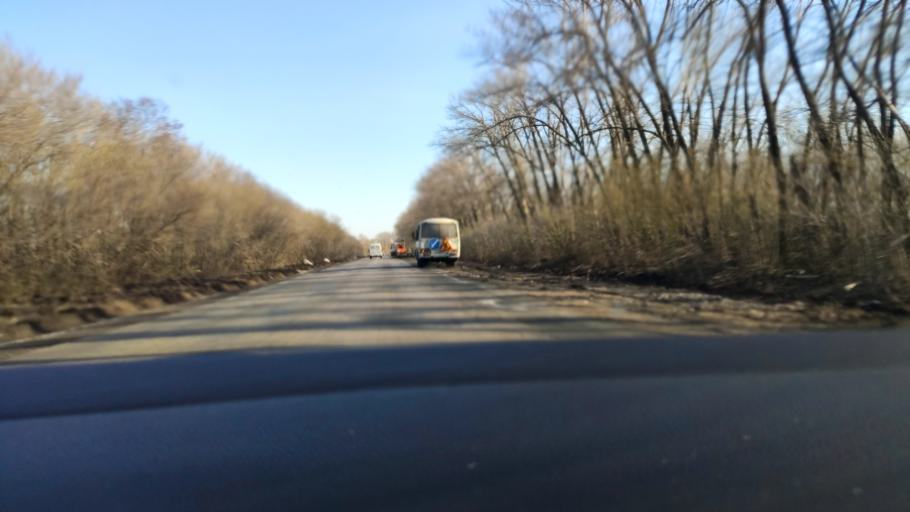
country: RU
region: Voronezj
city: Uryv-Pokrovka
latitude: 51.1978
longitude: 39.0827
